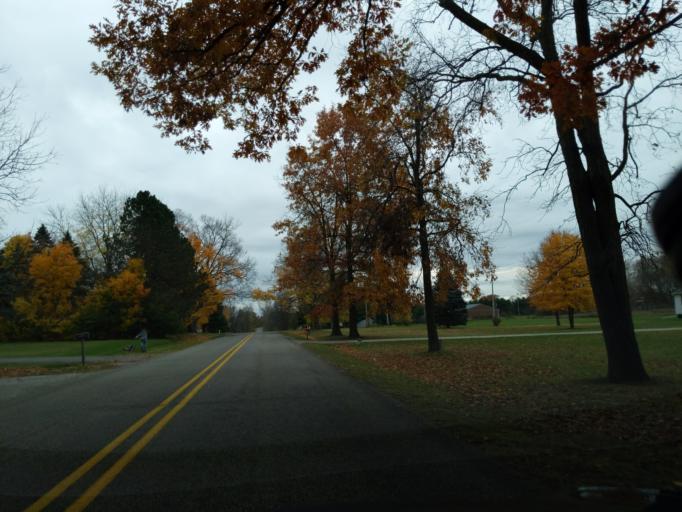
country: US
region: Michigan
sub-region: Eaton County
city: Eaton Rapids
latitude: 42.5215
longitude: -84.6015
